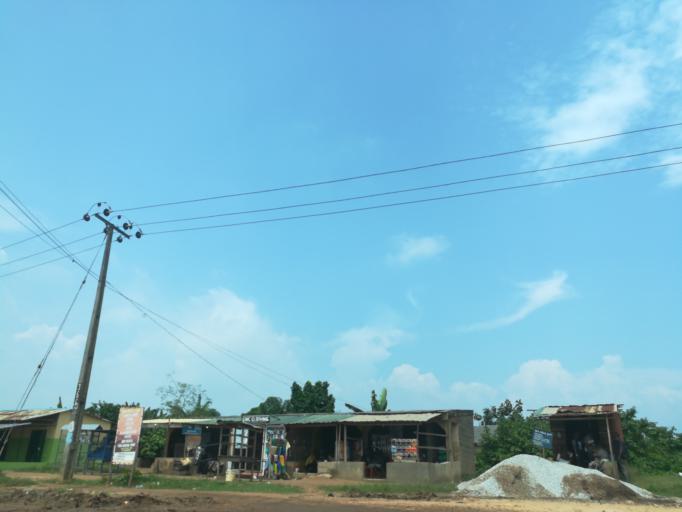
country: NG
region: Lagos
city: Ikorodu
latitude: 6.5885
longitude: 3.6244
